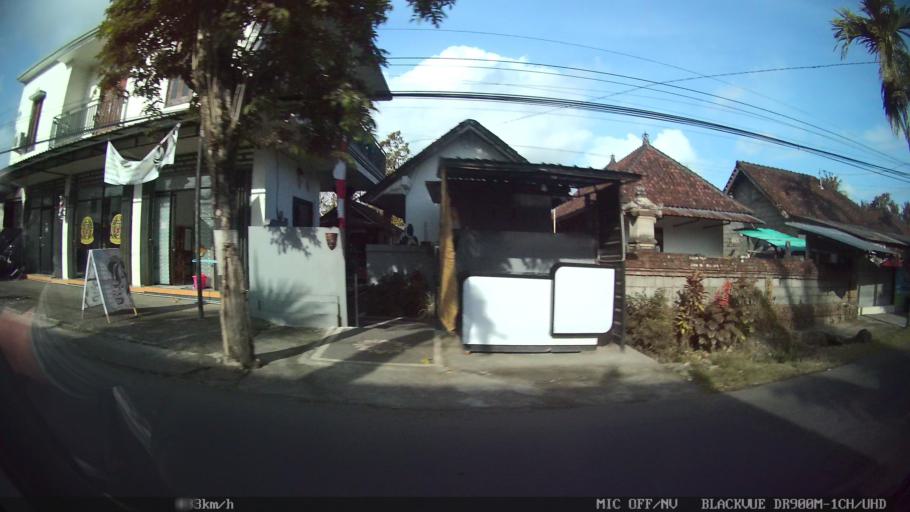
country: ID
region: Bali
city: Banjar Sedang
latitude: -8.5743
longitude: 115.2381
